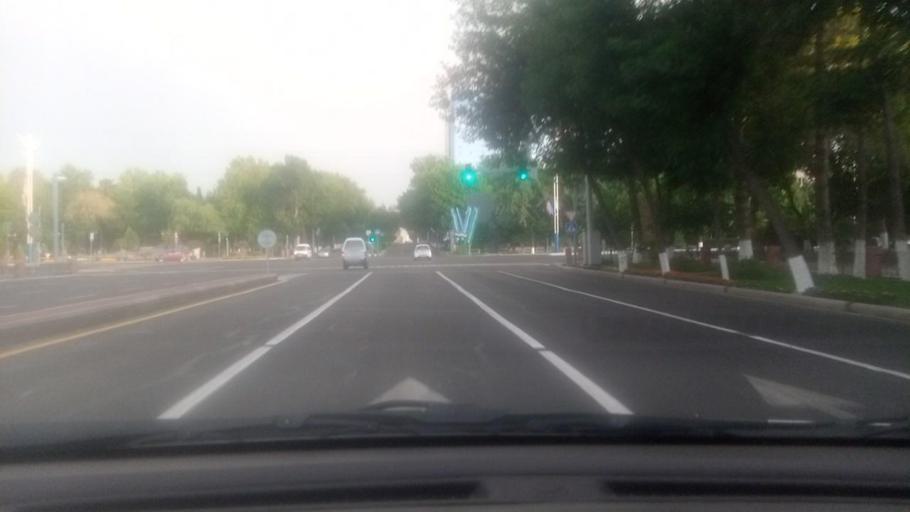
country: UZ
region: Toshkent
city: Salor
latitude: 41.3380
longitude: 69.3400
